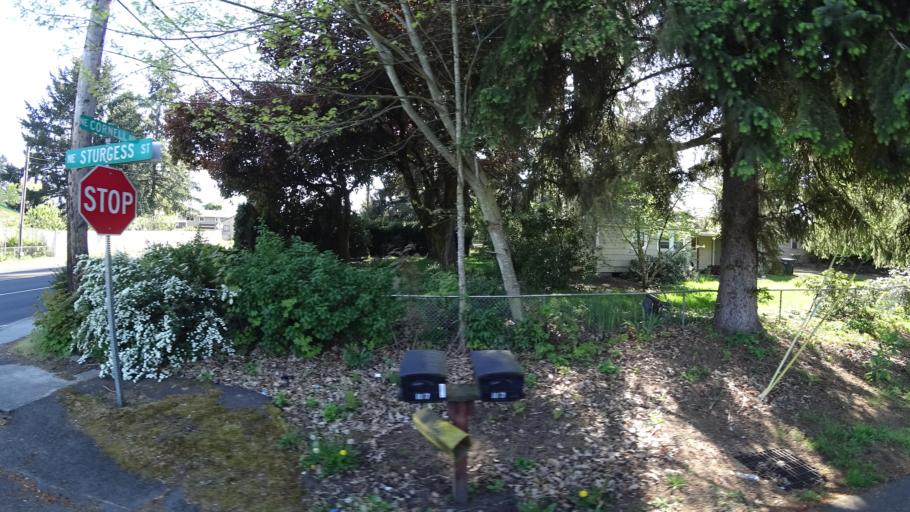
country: US
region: Oregon
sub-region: Washington County
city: Hillsboro
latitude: 45.5255
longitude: -122.9708
